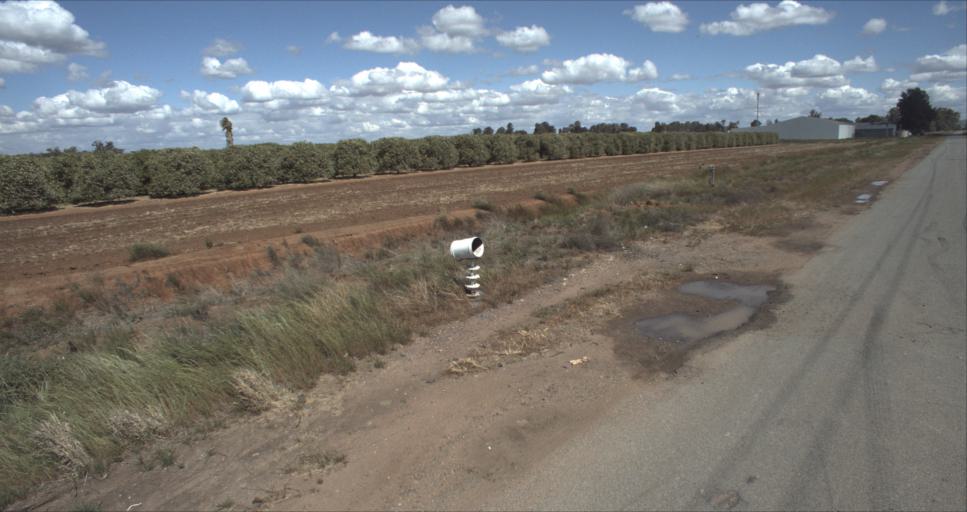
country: AU
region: New South Wales
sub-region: Leeton
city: Leeton
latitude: -34.5090
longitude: 146.2544
